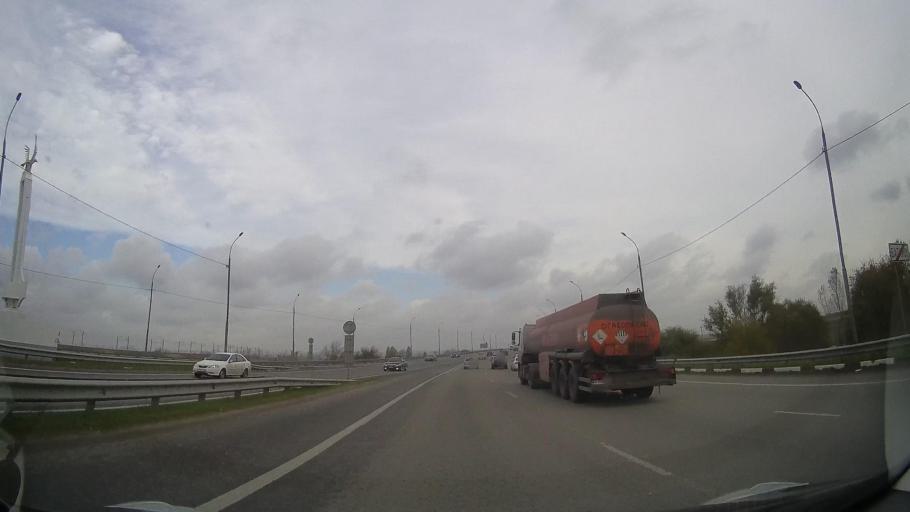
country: RU
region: Rostov
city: Bataysk
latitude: 47.1623
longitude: 39.7411
